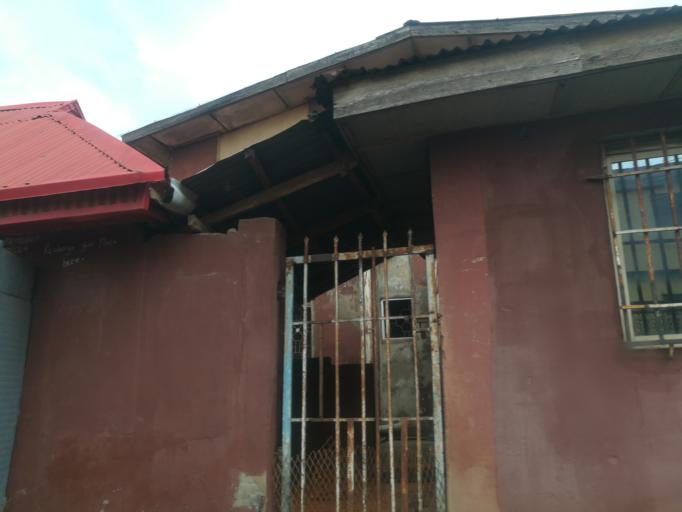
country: NG
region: Oyo
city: Ibadan
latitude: 7.4131
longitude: 3.9508
